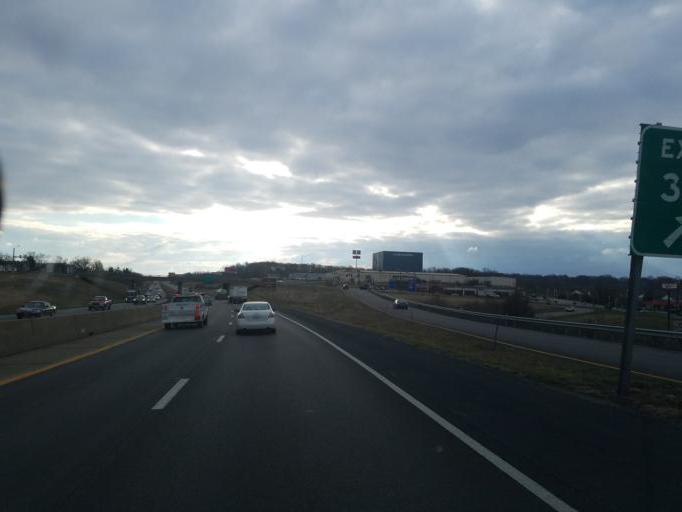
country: US
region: Missouri
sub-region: Saint Louis County
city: Glasgow Village
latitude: 38.7672
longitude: -90.2055
